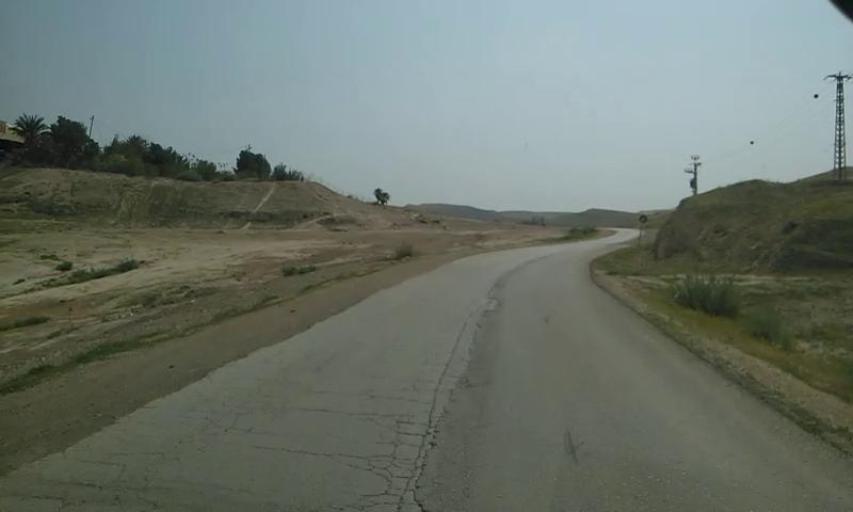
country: PS
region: West Bank
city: Jericho
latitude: 31.7873
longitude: 35.4306
